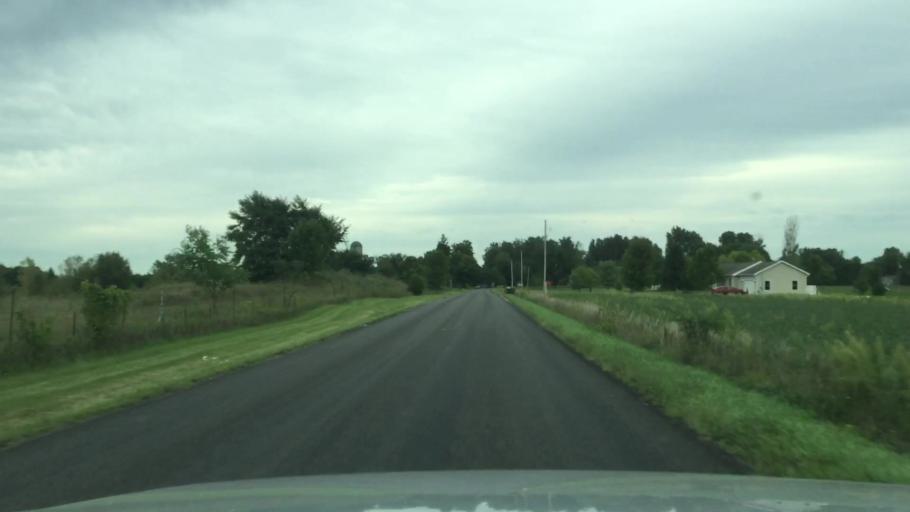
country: US
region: Michigan
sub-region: Shiawassee County
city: Durand
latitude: 42.8760
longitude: -84.0603
